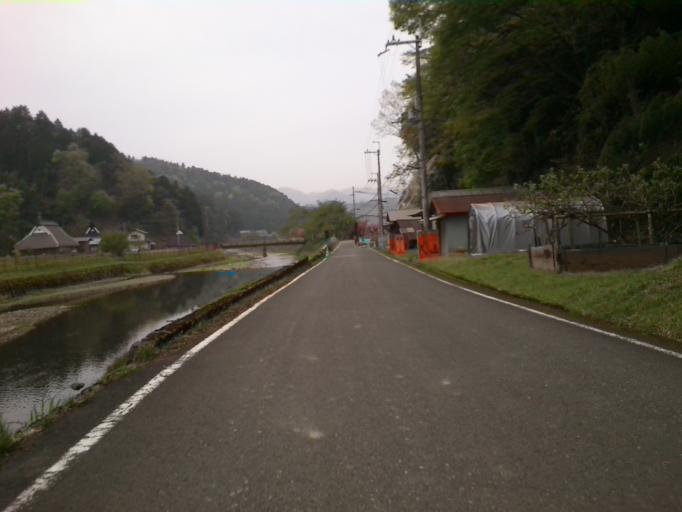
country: JP
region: Kyoto
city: Maizuru
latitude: 35.3677
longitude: 135.4565
